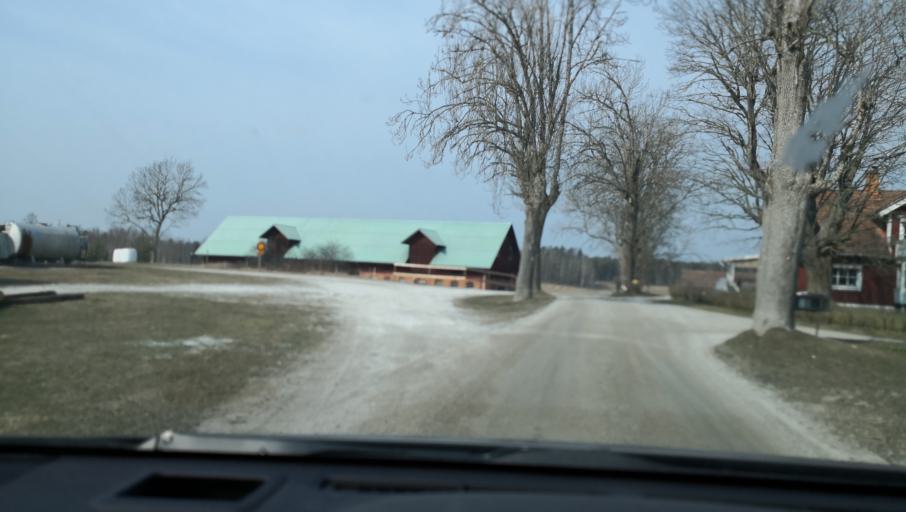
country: SE
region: OErebro
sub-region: Lindesbergs Kommun
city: Frovi
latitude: 59.3509
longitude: 15.4369
